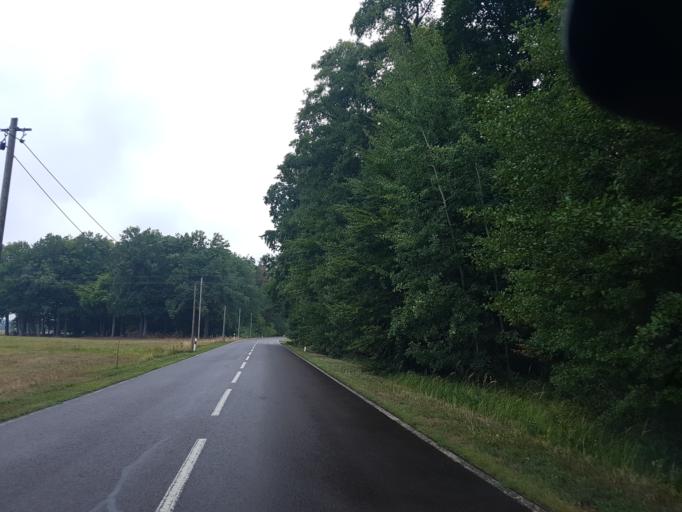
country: DE
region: Saxony-Anhalt
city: Tucheim
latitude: 52.2357
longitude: 12.1911
